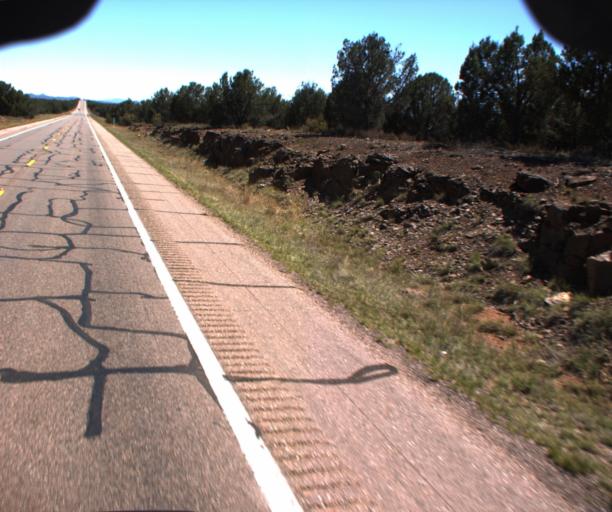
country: US
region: Arizona
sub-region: Yavapai County
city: Paulden
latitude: 35.0225
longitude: -112.3929
